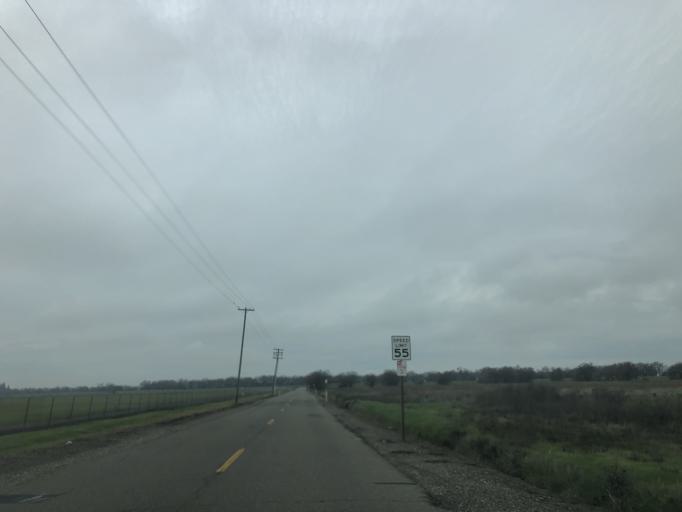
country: US
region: California
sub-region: Sacramento County
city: Elverta
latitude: 38.7144
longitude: -121.5956
